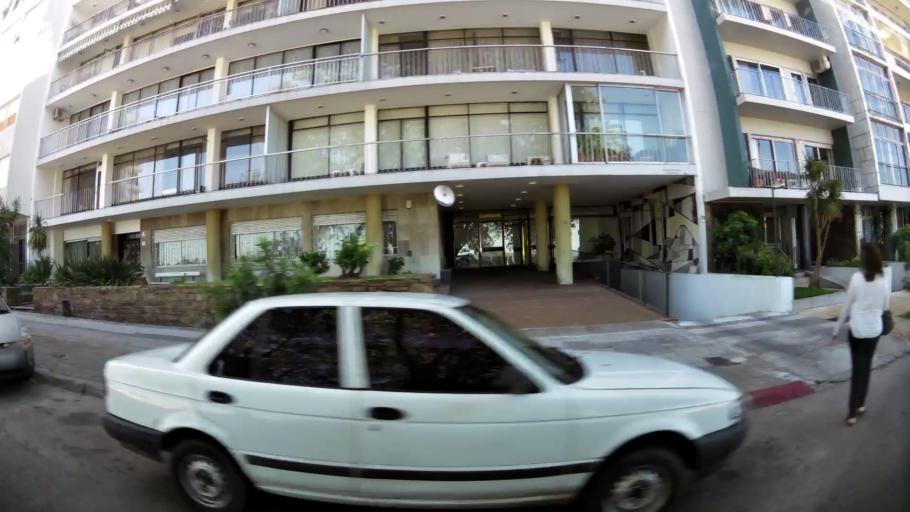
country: UY
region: Montevideo
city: Montevideo
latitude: -34.9104
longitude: -56.1448
